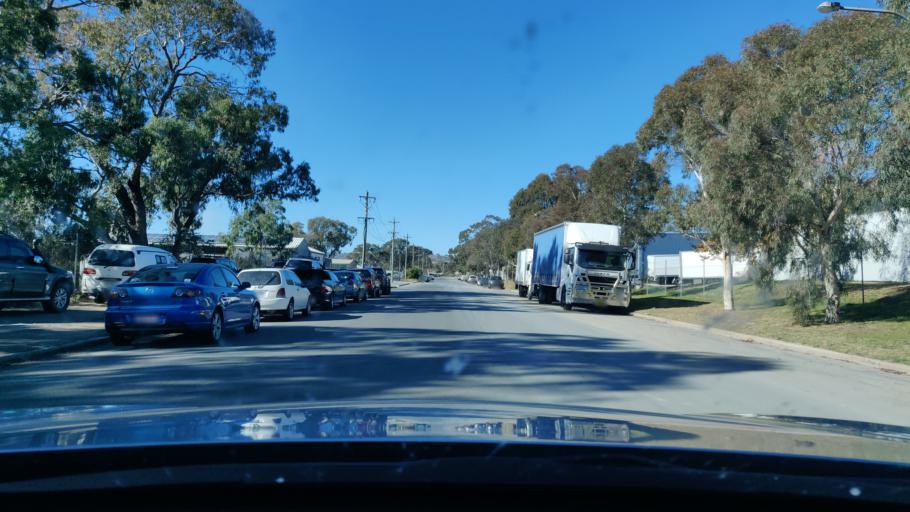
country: AU
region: Australian Capital Territory
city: Macarthur
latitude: -35.4008
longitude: 149.1573
